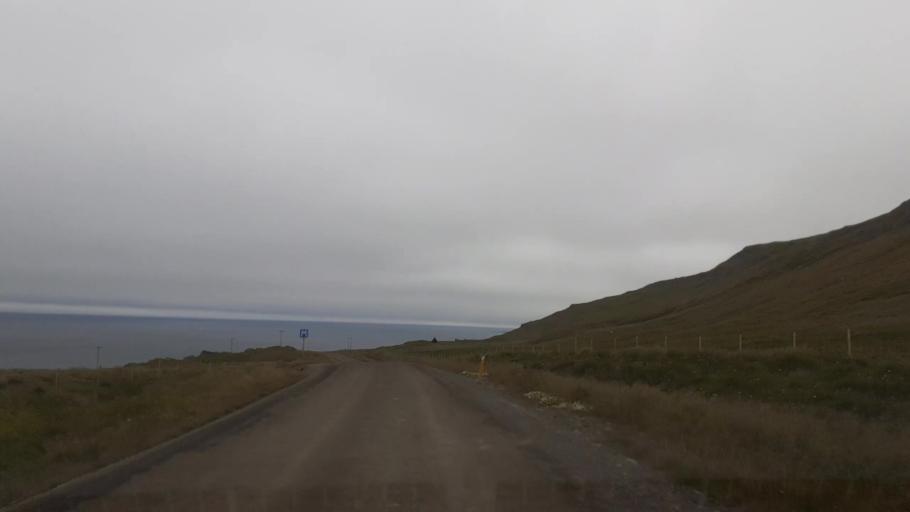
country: IS
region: Northwest
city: Saudarkrokur
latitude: 65.5100
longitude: -20.9710
